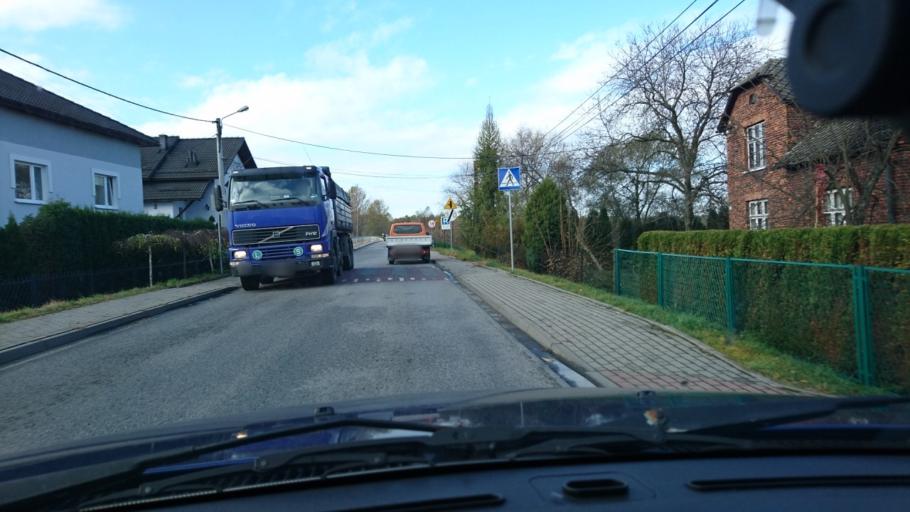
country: PL
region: Lesser Poland Voivodeship
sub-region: Powiat oswiecimski
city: Nowa Wies
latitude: 49.9382
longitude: 19.1985
